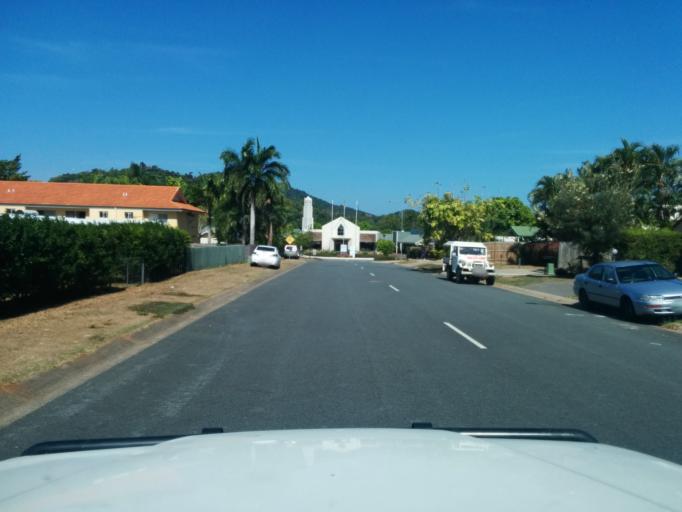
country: AU
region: Queensland
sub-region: Cairns
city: Redlynch
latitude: -16.8891
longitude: 145.6969
